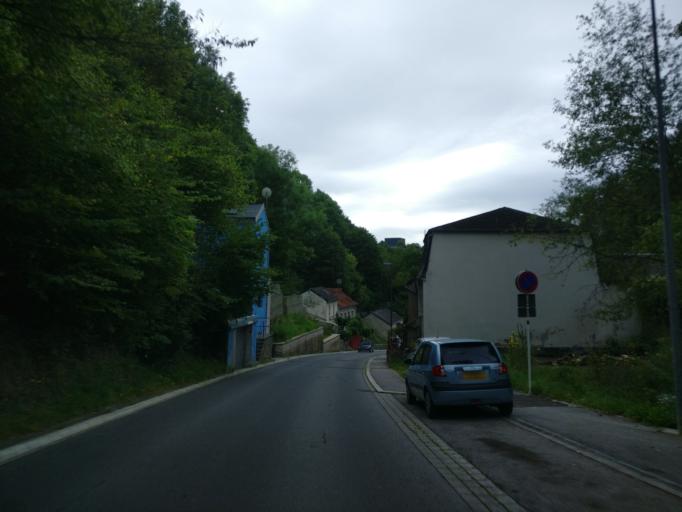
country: LU
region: Luxembourg
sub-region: Canton de Luxembourg
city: Luxembourg
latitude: 49.6216
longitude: 6.1370
